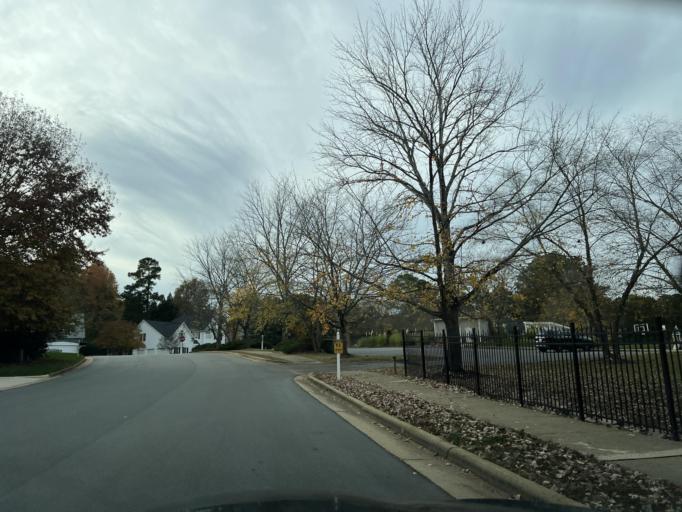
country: US
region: North Carolina
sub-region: Wake County
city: Wake Forest
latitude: 35.8929
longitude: -78.5927
